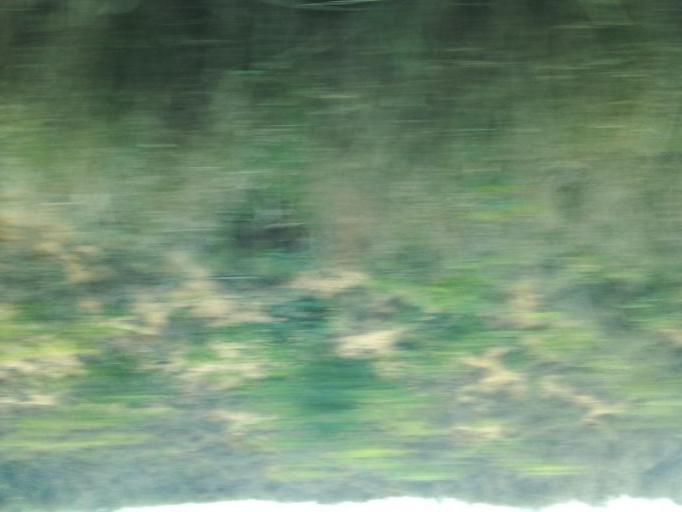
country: BR
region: Minas Gerais
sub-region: Belo Oriente
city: Belo Oriente
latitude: -19.2229
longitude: -42.3001
